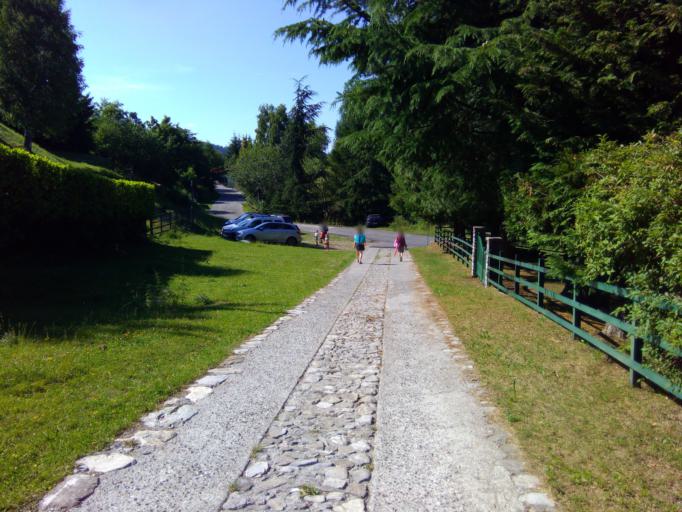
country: IT
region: Lombardy
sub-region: Provincia di Como
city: Casasco Intelvi
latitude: 45.9450
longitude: 9.0686
